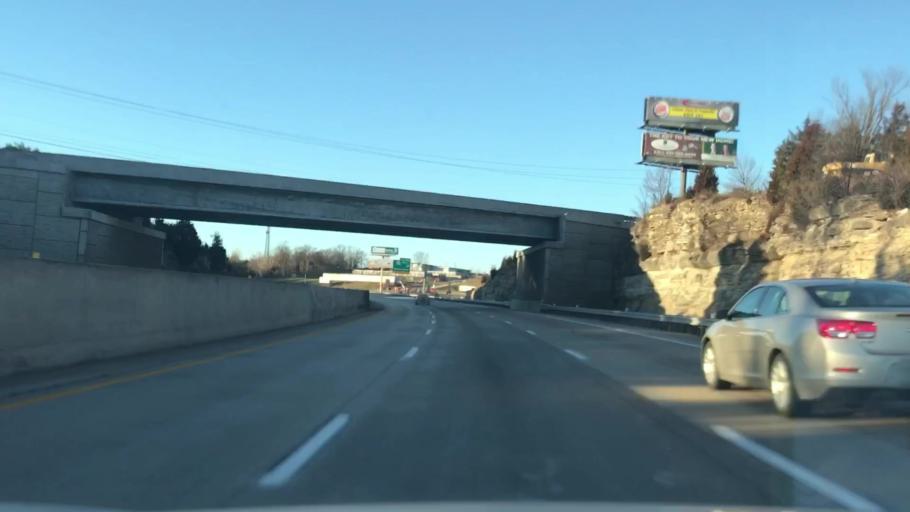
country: US
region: Missouri
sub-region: Franklin County
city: Gray Summit
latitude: 38.4814
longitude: -90.8451
